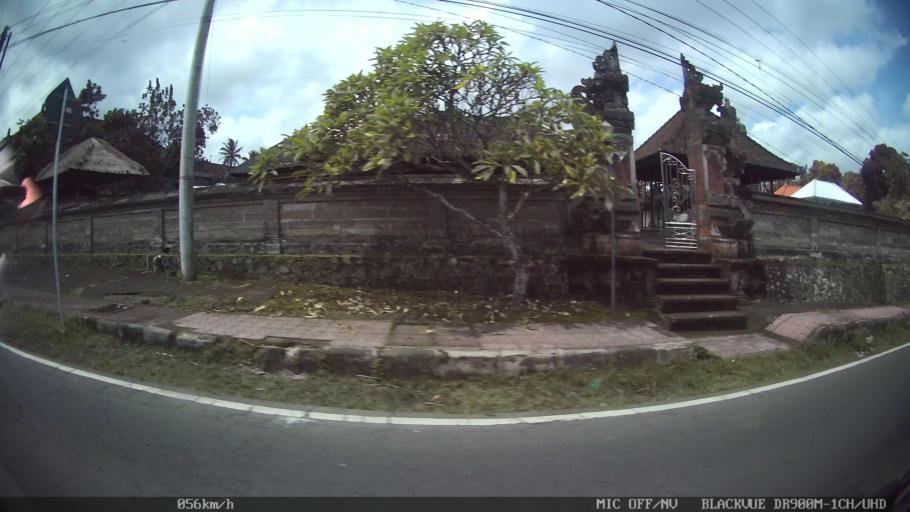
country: ID
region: Bali
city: Banjar Wangsian
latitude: -8.4943
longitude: 115.4029
